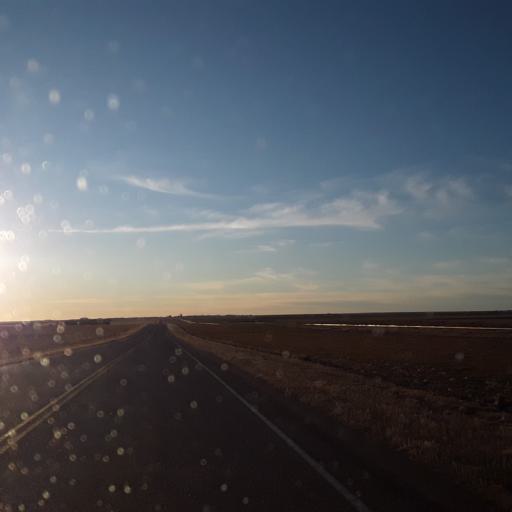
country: US
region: Colorado
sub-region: Cheyenne County
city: Cheyenne Wells
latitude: 38.8477
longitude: -102.2431
